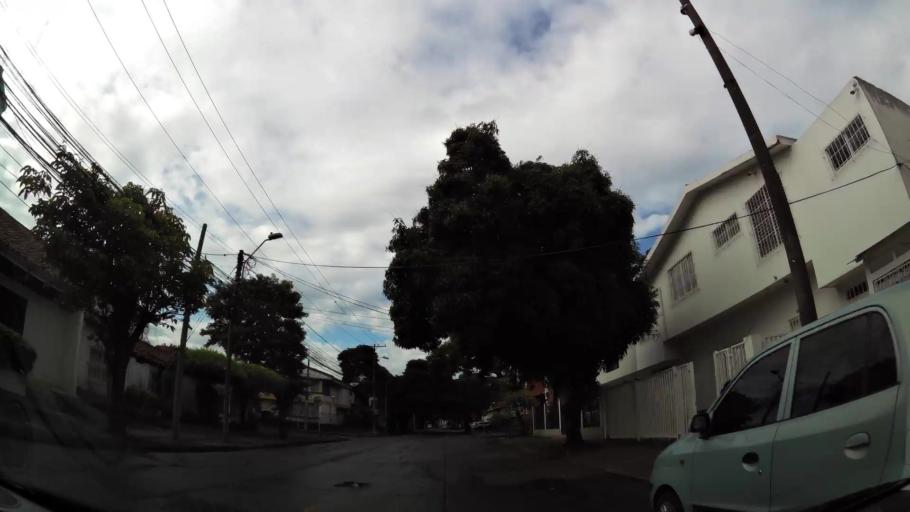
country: CO
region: Valle del Cauca
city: Cali
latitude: 3.4740
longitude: -76.5218
